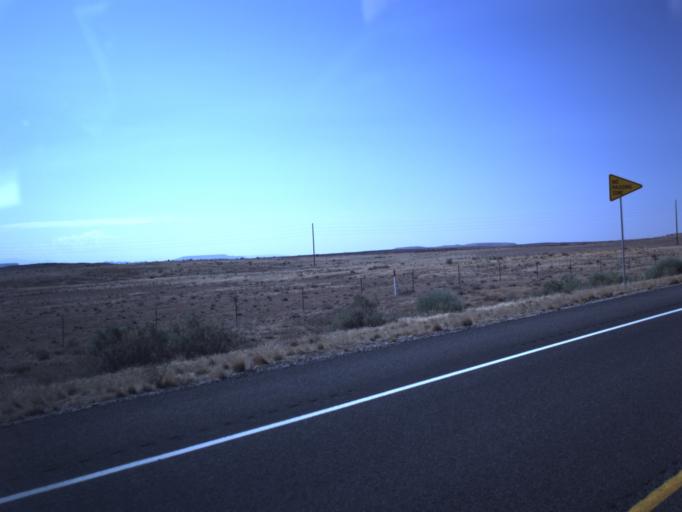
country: US
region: Utah
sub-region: San Juan County
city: Blanding
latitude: 37.4168
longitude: -109.4791
